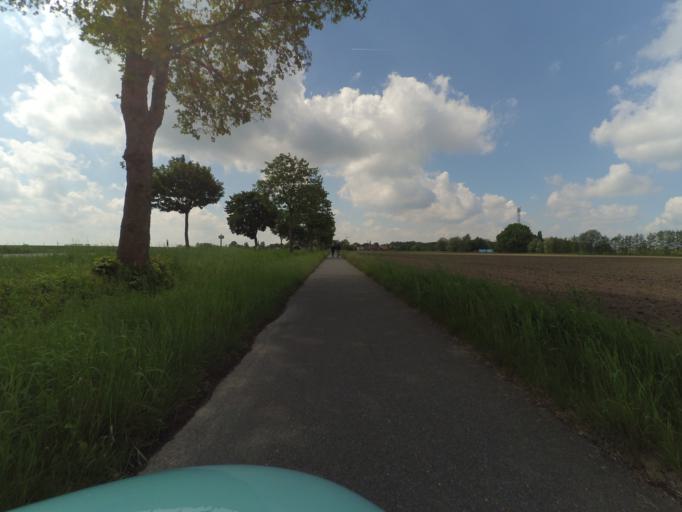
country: DE
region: Lower Saxony
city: Lengede
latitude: 52.2626
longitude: 10.2818
